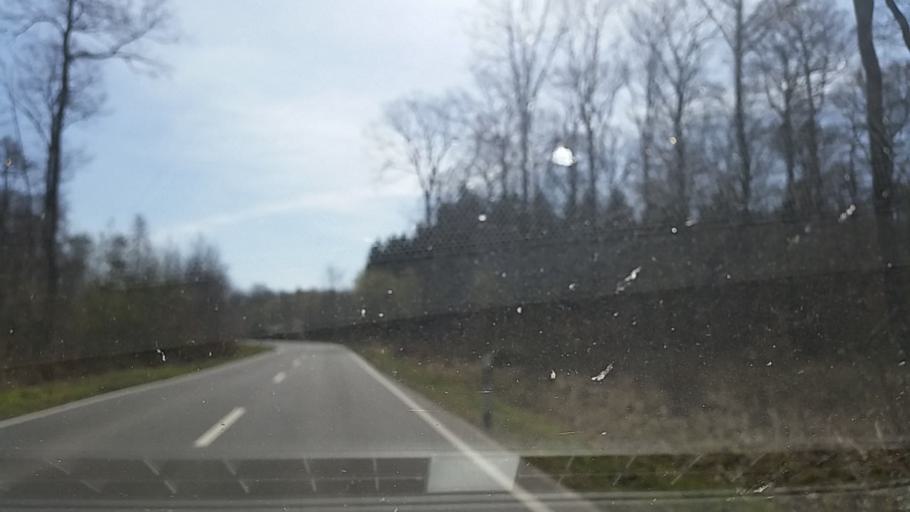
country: DE
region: Lower Saxony
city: Warberg
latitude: 52.1648
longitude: 10.8929
